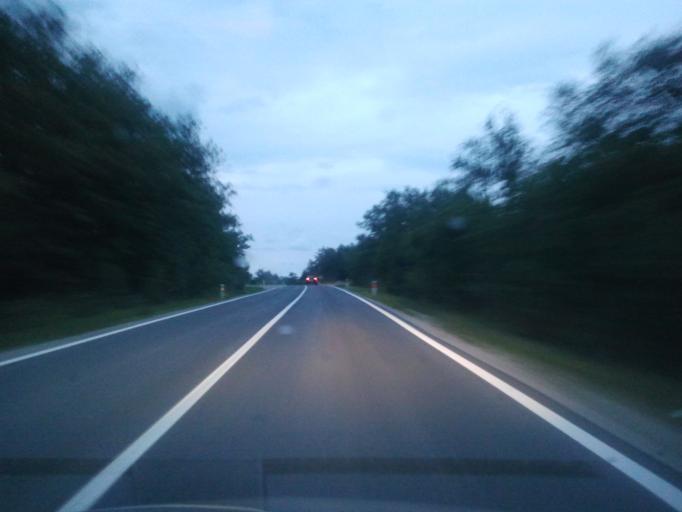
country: HR
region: Zadarska
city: Gracac
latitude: 44.4502
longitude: 15.8378
